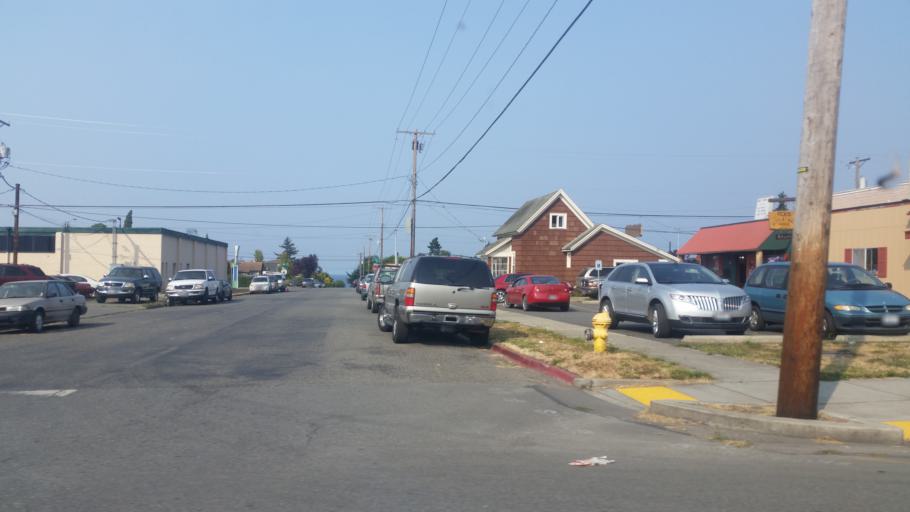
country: US
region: Washington
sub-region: Clallam County
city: Port Angeles
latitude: 48.1138
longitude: -123.4207
